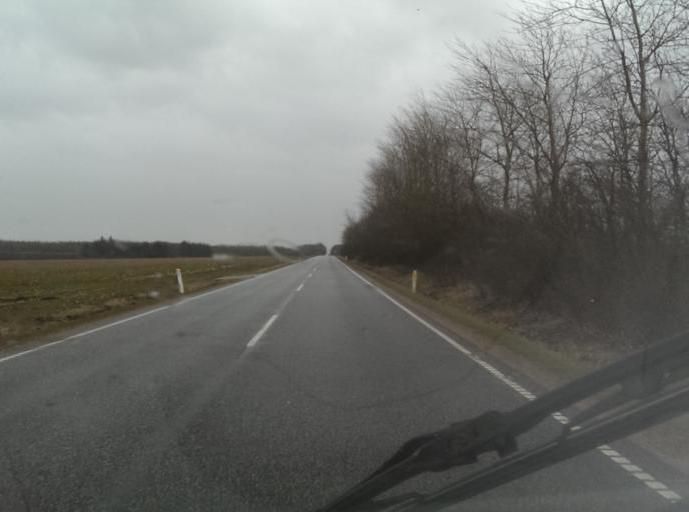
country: DK
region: Central Jutland
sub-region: Ringkobing-Skjern Kommune
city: Skjern
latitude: 56.0830
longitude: 8.4116
